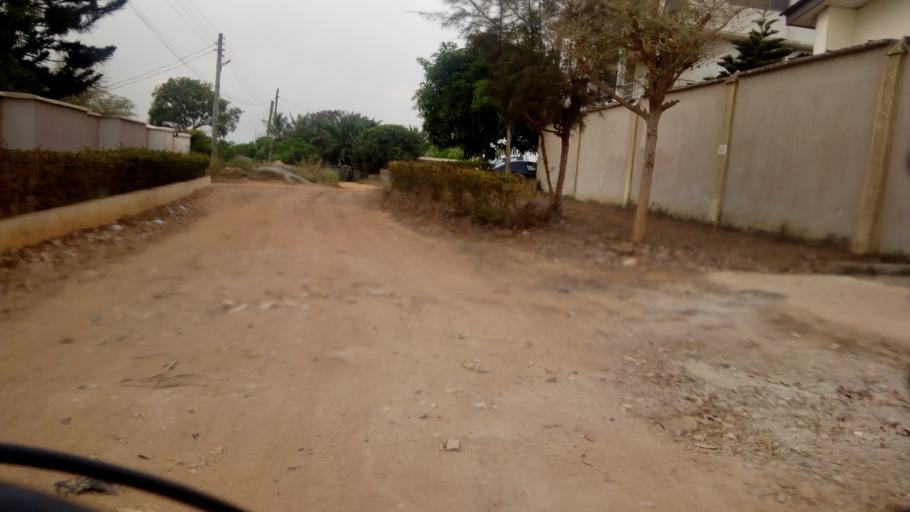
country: GH
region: Central
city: Cape Coast
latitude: 5.1100
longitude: -1.2761
